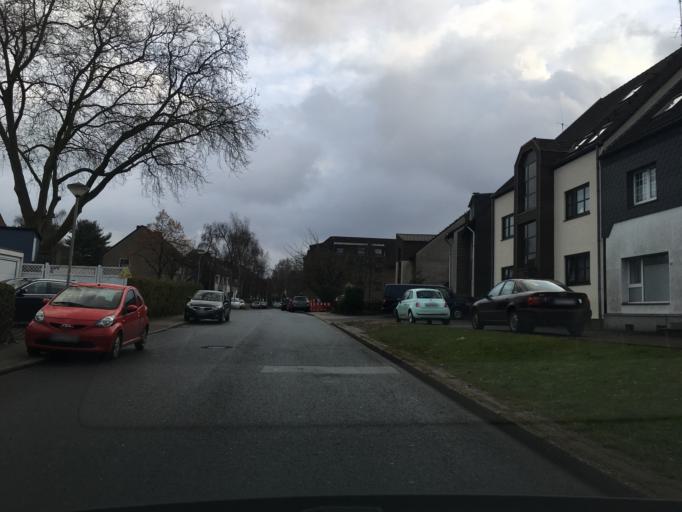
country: DE
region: North Rhine-Westphalia
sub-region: Regierungsbezirk Dusseldorf
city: Oberhausen
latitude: 51.4549
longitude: 6.8407
